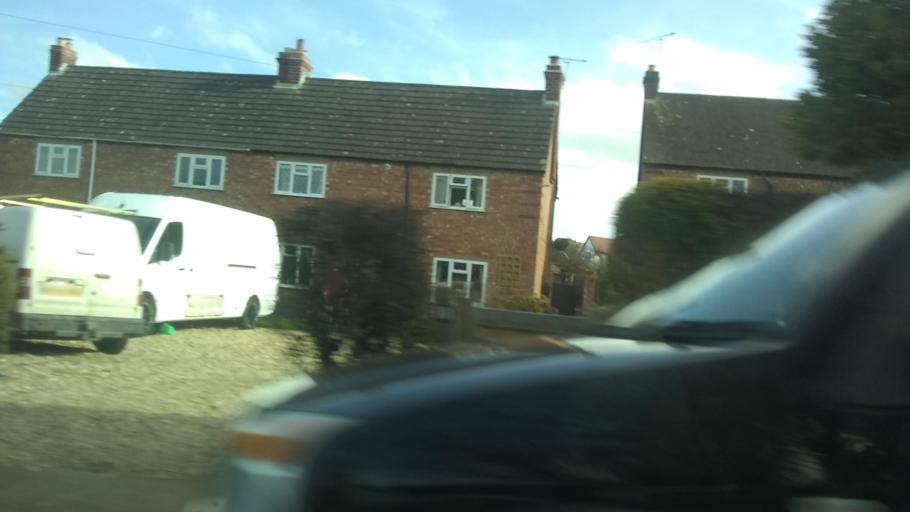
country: GB
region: England
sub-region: Shropshire
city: Highley
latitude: 52.3701
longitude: -2.3985
